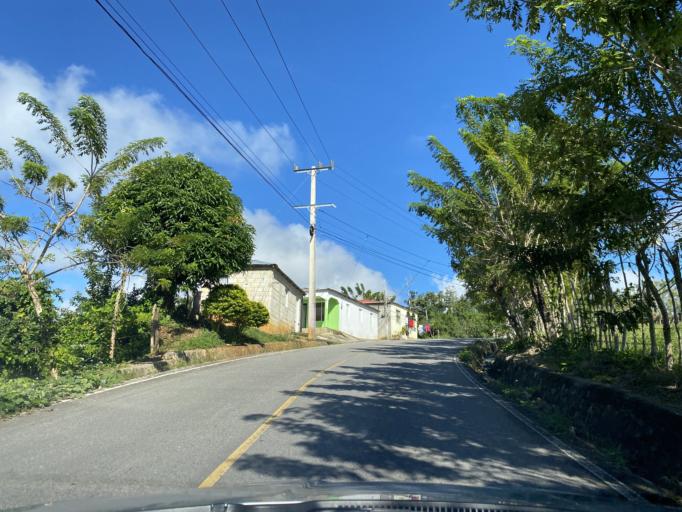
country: DO
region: Samana
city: Sanchez
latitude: 19.2512
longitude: -69.5884
